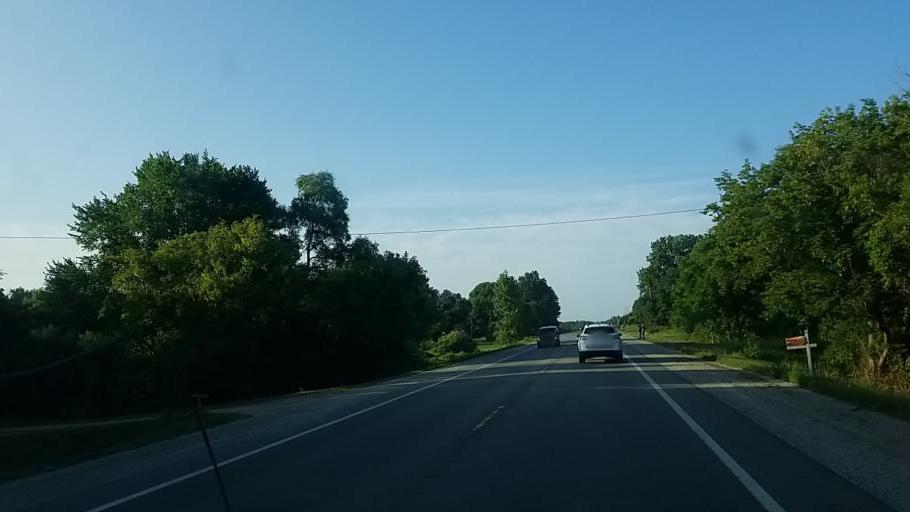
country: US
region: Michigan
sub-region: Montcalm County
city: Stanton
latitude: 43.2408
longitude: -85.0735
